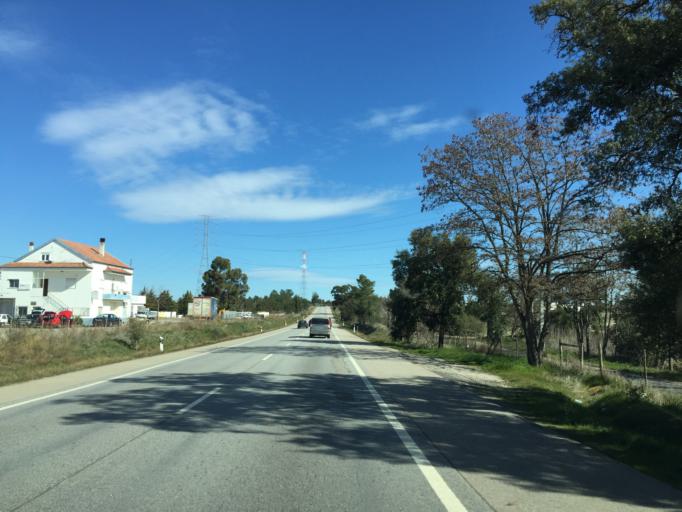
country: PT
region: Castelo Branco
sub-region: Castelo Branco
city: Castelo Branco
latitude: 39.7881
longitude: -7.5633
